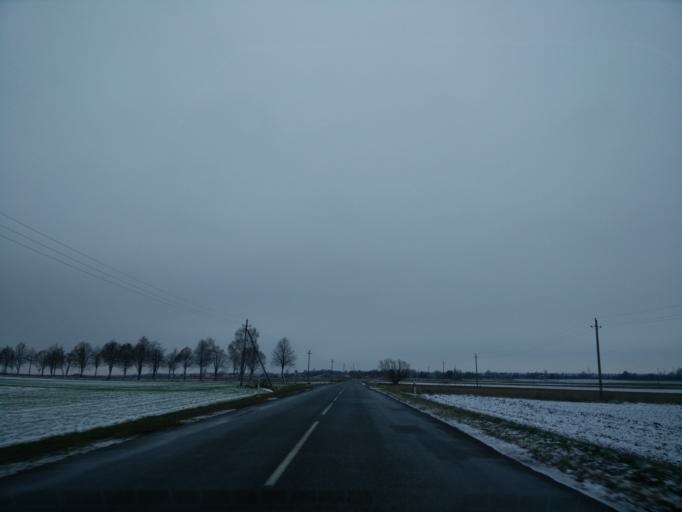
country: LT
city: Ariogala
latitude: 55.3516
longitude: 23.3832
